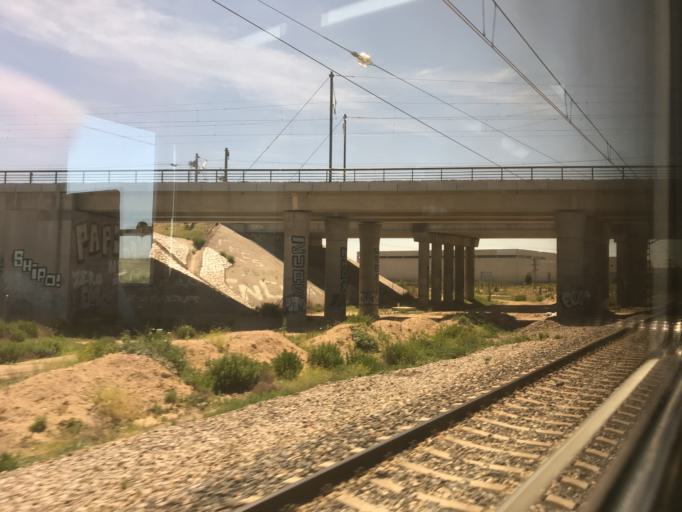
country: ES
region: Madrid
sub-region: Provincia de Madrid
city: Getafe
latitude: 40.2829
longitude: -3.7042
